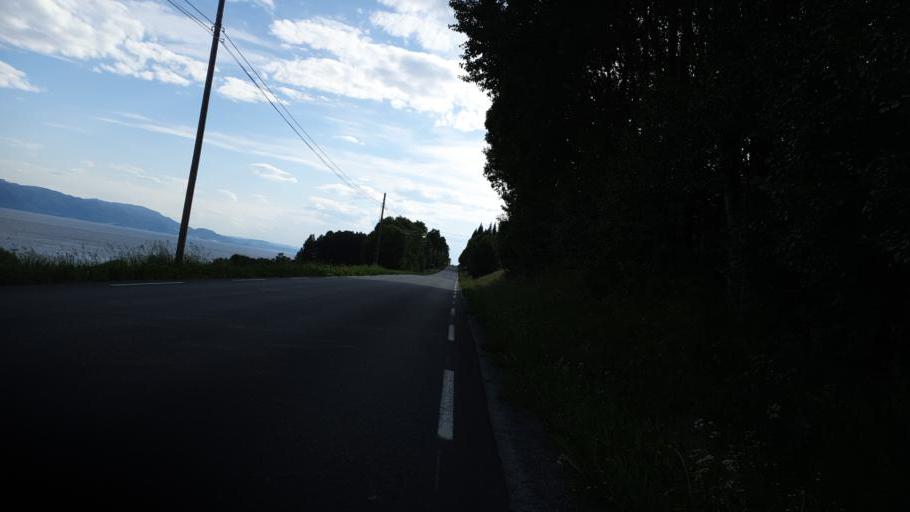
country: NO
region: Sor-Trondelag
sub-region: Trondheim
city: Trondheim
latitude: 63.5608
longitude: 10.3179
